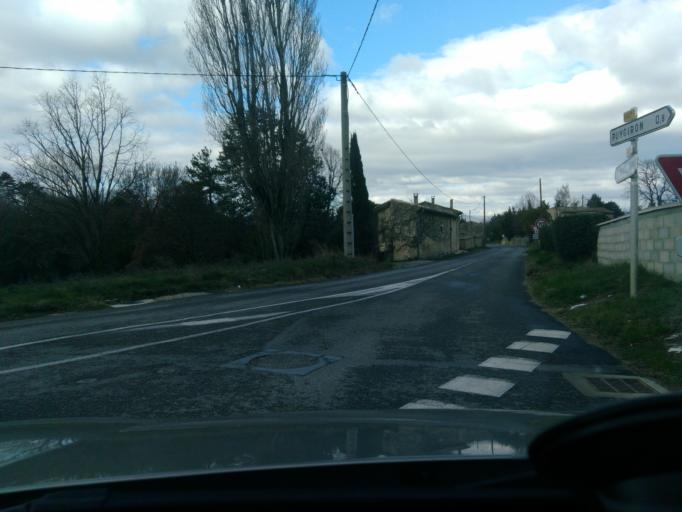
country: FR
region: Rhone-Alpes
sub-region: Departement de la Drome
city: Montboucher-sur-Jabron
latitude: 44.5428
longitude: 4.8440
